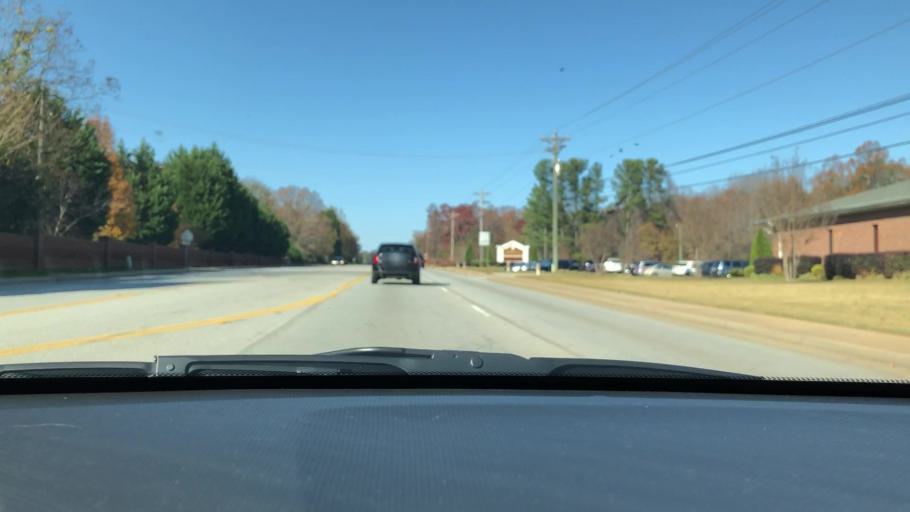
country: US
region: South Carolina
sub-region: Greenville County
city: Five Forks
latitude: 34.8093
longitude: -82.2374
